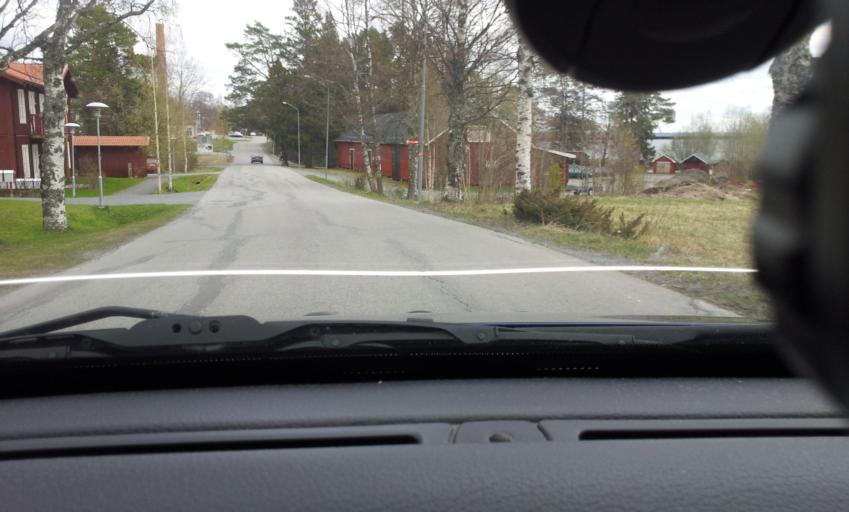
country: SE
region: Jaemtland
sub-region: OEstersunds Kommun
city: Ostersund
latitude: 63.1662
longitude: 14.5924
